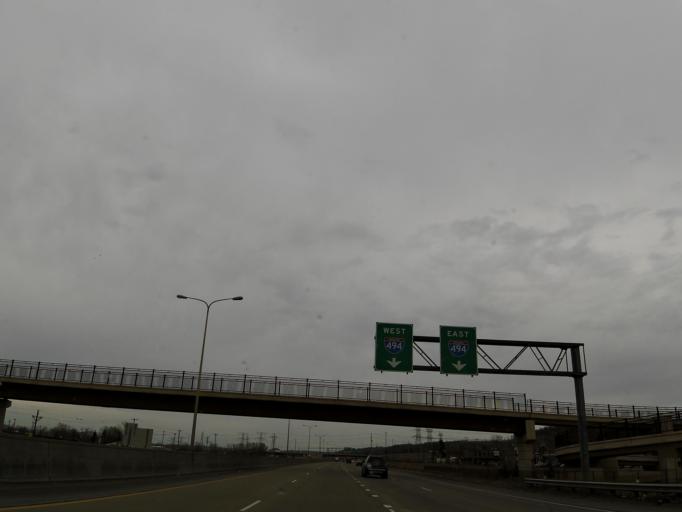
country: US
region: Minnesota
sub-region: Washington County
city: Newport
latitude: 44.8774
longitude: -93.0022
